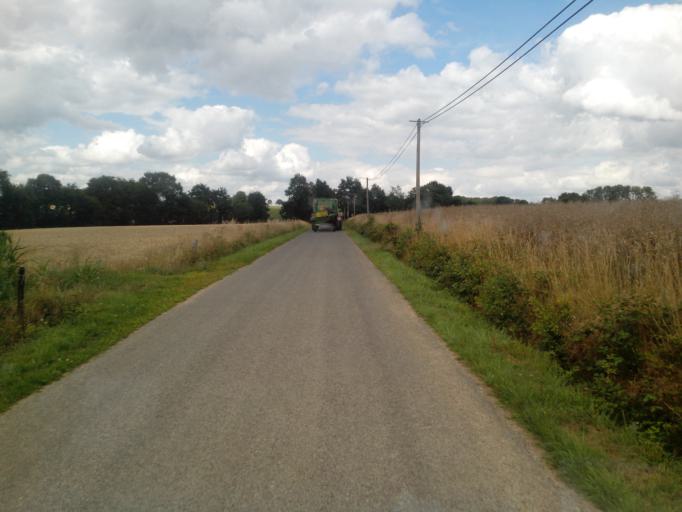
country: FR
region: Brittany
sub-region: Departement du Morbihan
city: Guilliers
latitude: 48.0980
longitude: -2.4044
